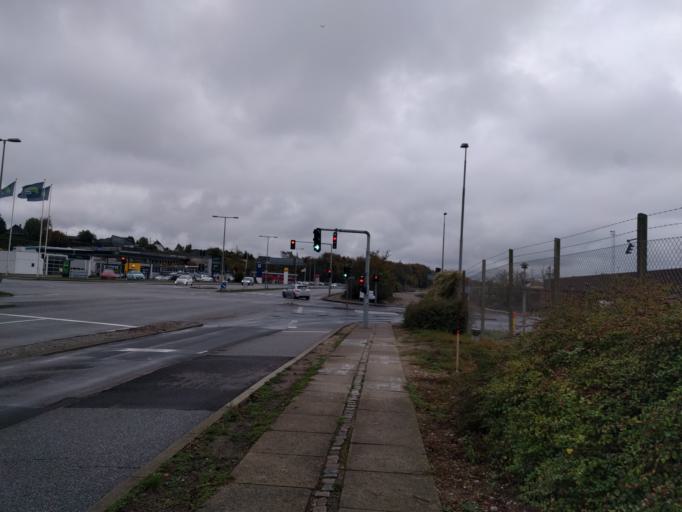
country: DK
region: South Denmark
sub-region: Fredericia Kommune
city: Fredericia
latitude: 55.5562
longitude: 9.7288
